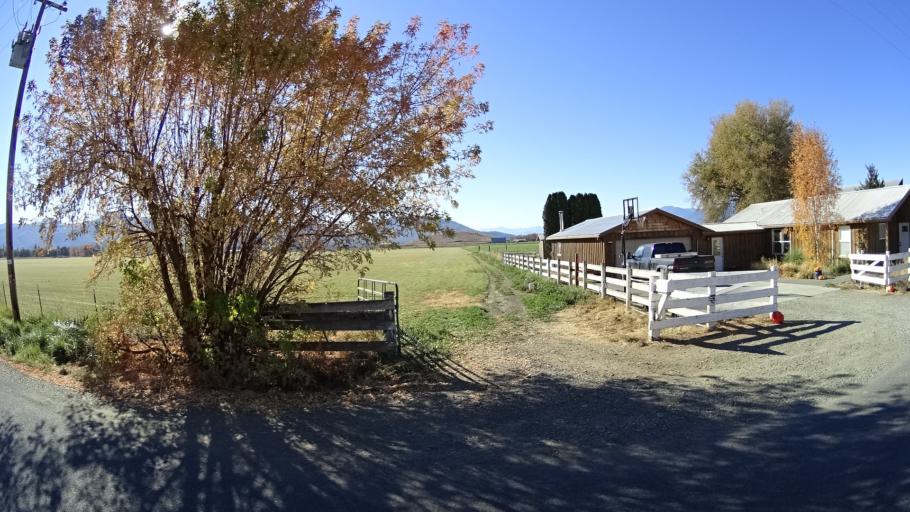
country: US
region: California
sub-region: Siskiyou County
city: Yreka
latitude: 41.5790
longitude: -122.8345
